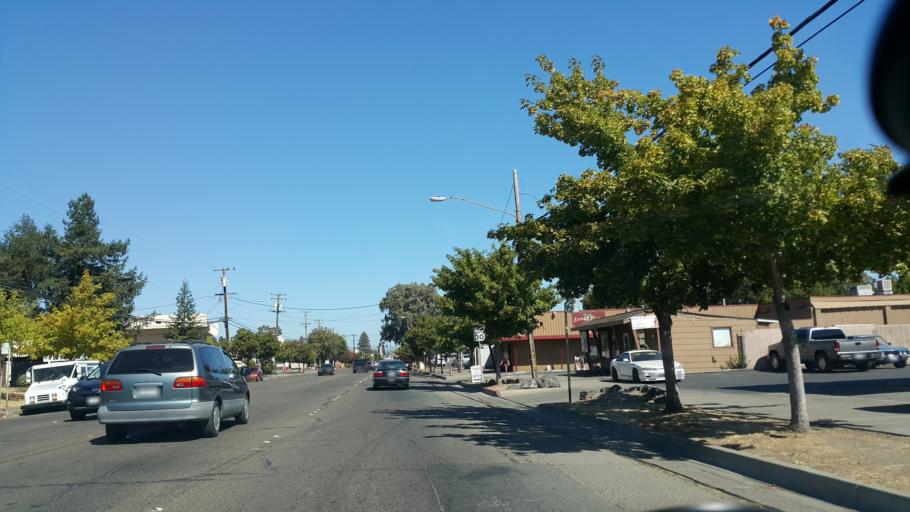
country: US
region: California
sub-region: Mendocino County
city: Ukiah
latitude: 39.1396
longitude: -123.2059
